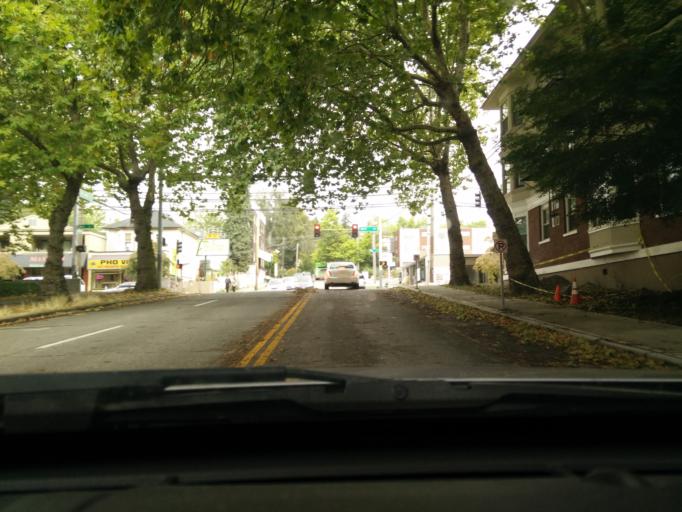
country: US
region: Washington
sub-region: King County
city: Seattle
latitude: 47.6250
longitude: -122.3488
